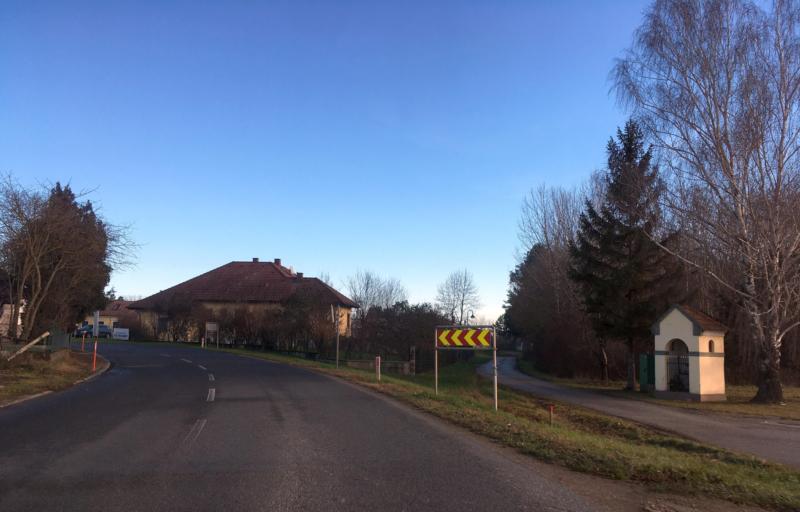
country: AT
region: Lower Austria
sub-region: Politischer Bezirk Bruck an der Leitha
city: Petronell-Carnuntum
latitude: 48.1472
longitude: 16.8337
